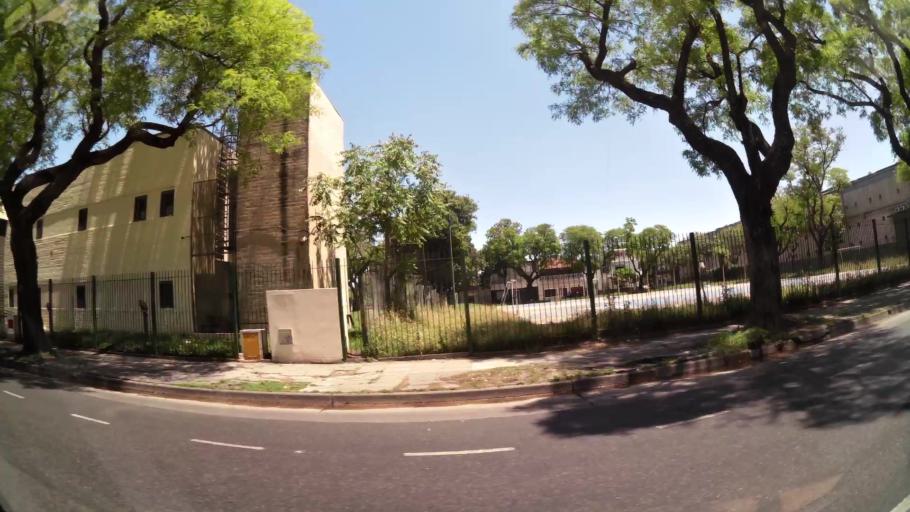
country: AR
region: Buenos Aires
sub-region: Partido de Avellaneda
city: Avellaneda
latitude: -34.6487
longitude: -58.3893
